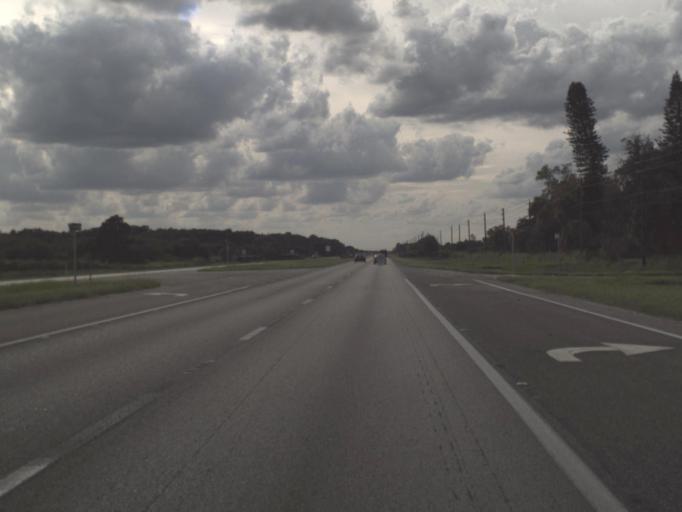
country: US
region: Florida
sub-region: Lee County
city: Alva
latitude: 26.7097
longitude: -81.5618
